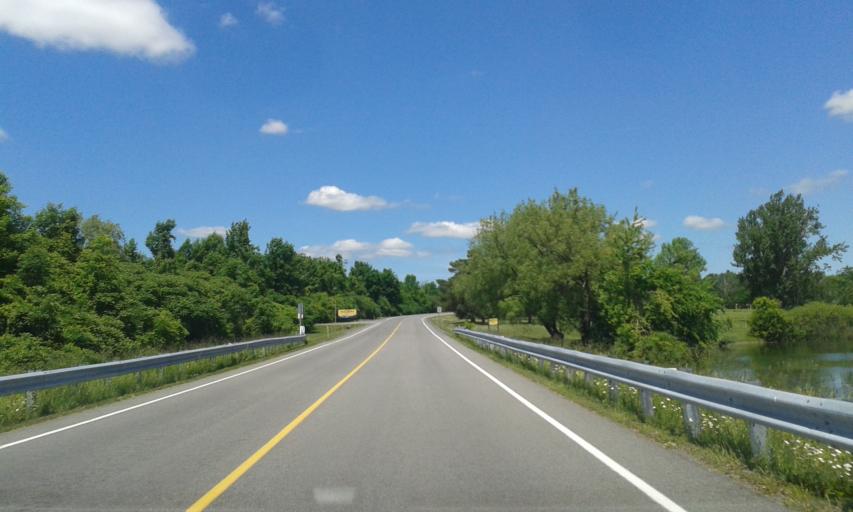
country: US
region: New York
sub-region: St. Lawrence County
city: Massena
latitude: 45.0103
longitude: -74.8954
